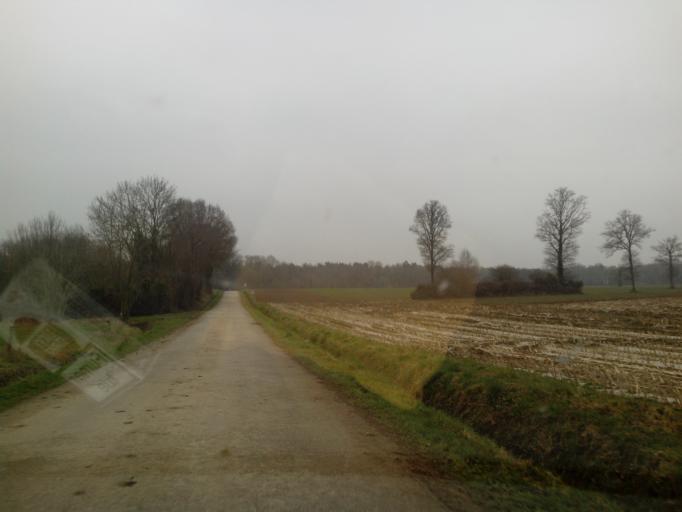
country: FR
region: Brittany
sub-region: Departement du Morbihan
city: Guilliers
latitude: 48.1066
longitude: -2.3824
